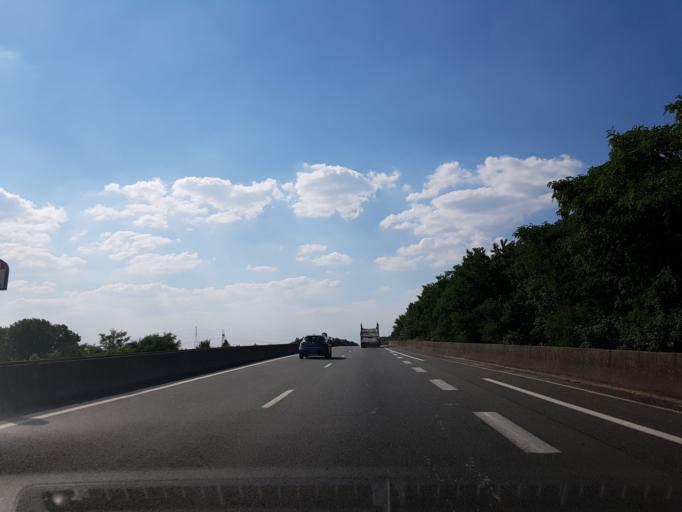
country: FR
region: Nord-Pas-de-Calais
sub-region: Departement du Nord
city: Escaudain
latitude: 50.3278
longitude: 3.3359
